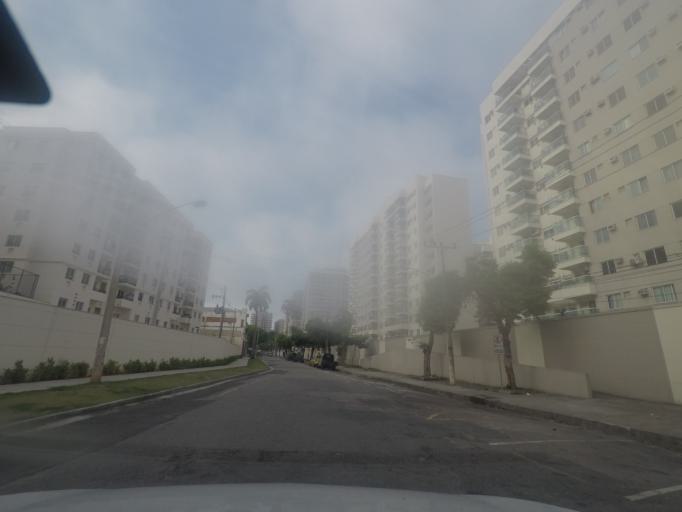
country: BR
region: Rio de Janeiro
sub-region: Duque De Caxias
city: Duque de Caxias
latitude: -22.8374
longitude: -43.2743
